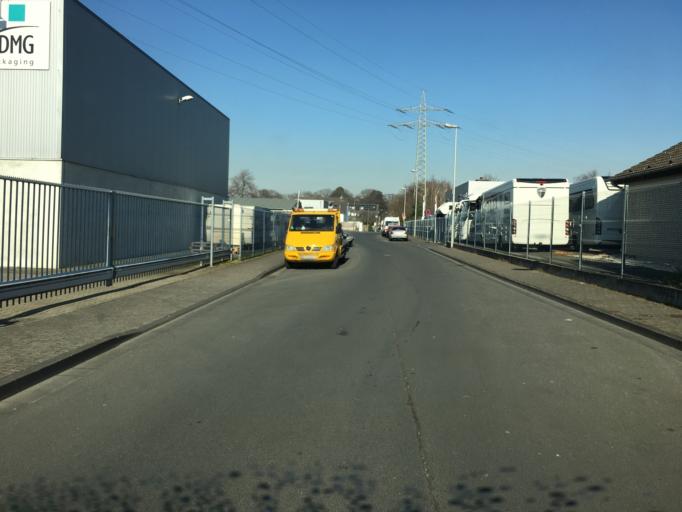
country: DE
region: North Rhine-Westphalia
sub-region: Regierungsbezirk Koln
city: Pulheim
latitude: 50.9603
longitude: 6.8038
